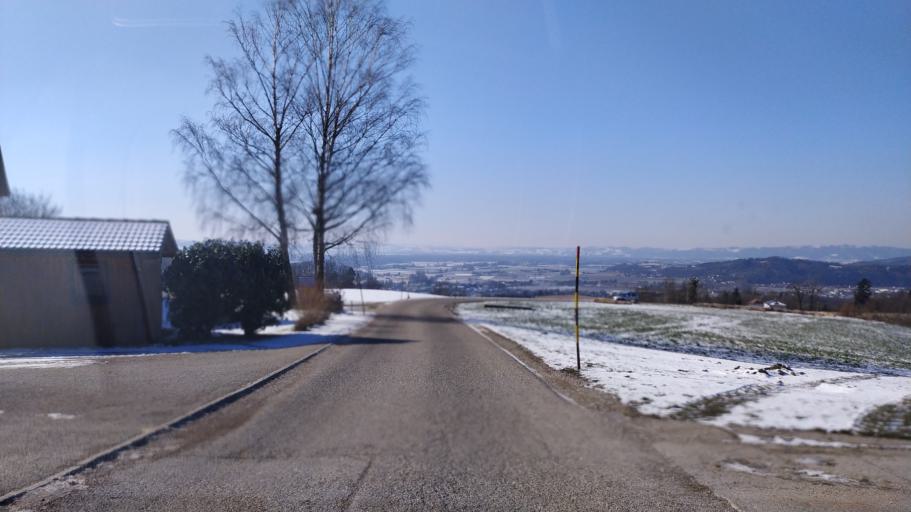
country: AT
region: Upper Austria
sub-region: Politischer Bezirk Urfahr-Umgebung
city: Ottensheim
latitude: 48.3452
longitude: 14.2004
